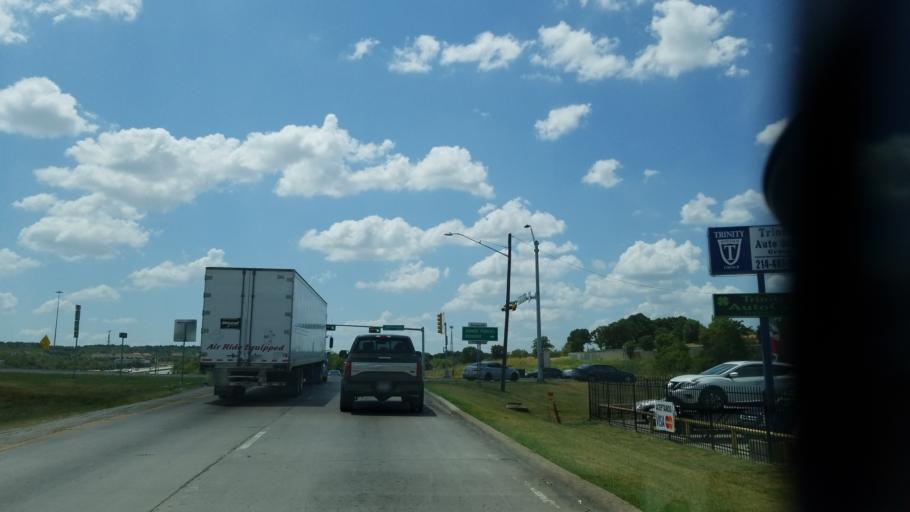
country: US
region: Texas
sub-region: Dallas County
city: Cockrell Hill
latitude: 32.7485
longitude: -96.9206
